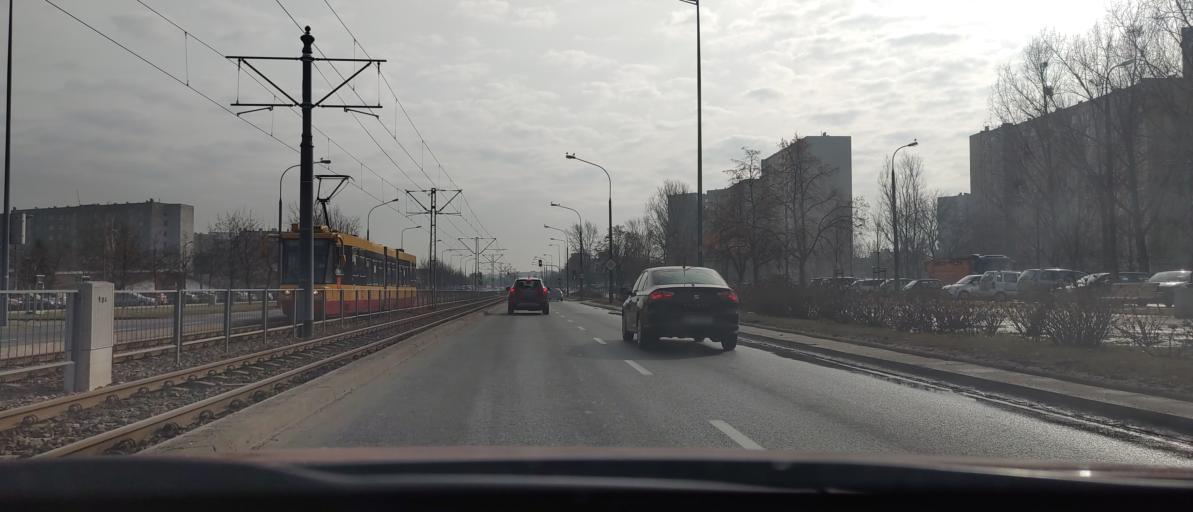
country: PL
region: Masovian Voivodeship
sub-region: Warszawa
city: Bemowo
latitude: 52.2509
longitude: 20.9162
